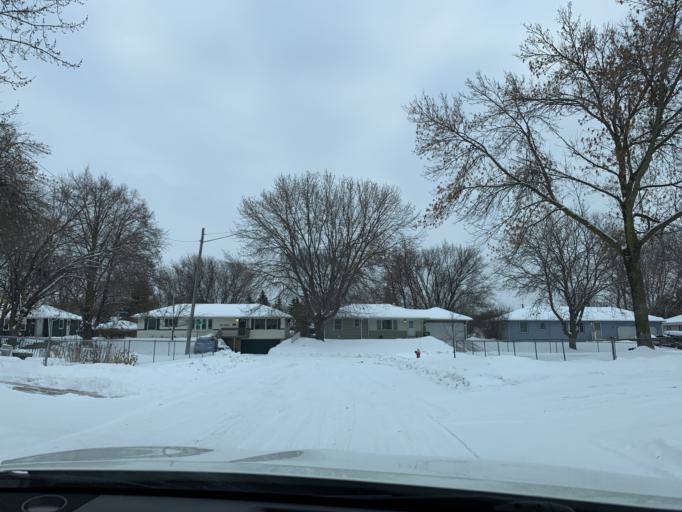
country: US
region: Minnesota
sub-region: Anoka County
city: Coon Rapids
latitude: 45.1666
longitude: -93.2859
